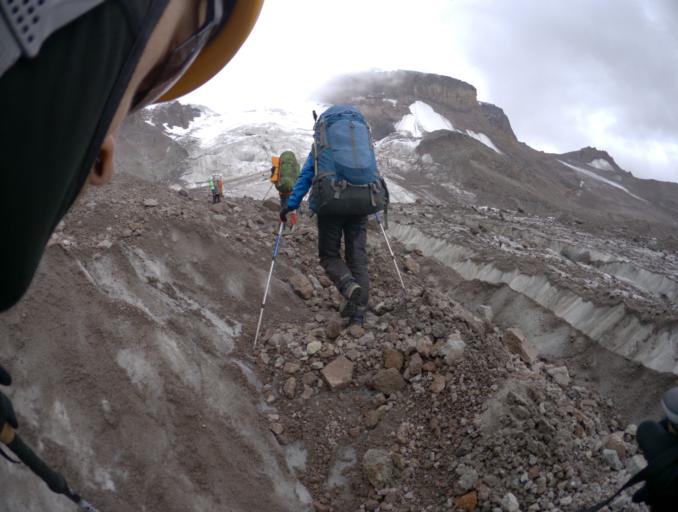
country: RU
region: Kabardino-Balkariya
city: Terskol
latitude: 43.3787
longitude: 42.3995
